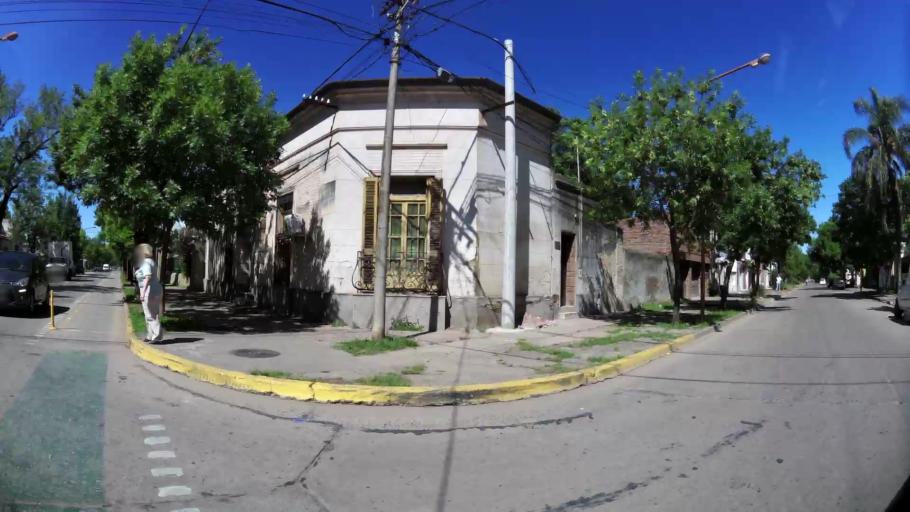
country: AR
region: Santa Fe
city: Esperanza
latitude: -31.4441
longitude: -60.9310
